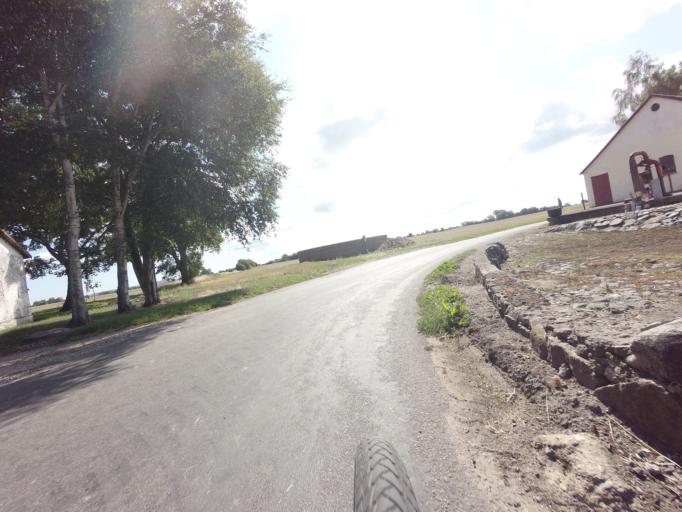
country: DK
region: Zealand
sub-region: Vordingborg Kommune
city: Stege
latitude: 54.9759
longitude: 12.3381
